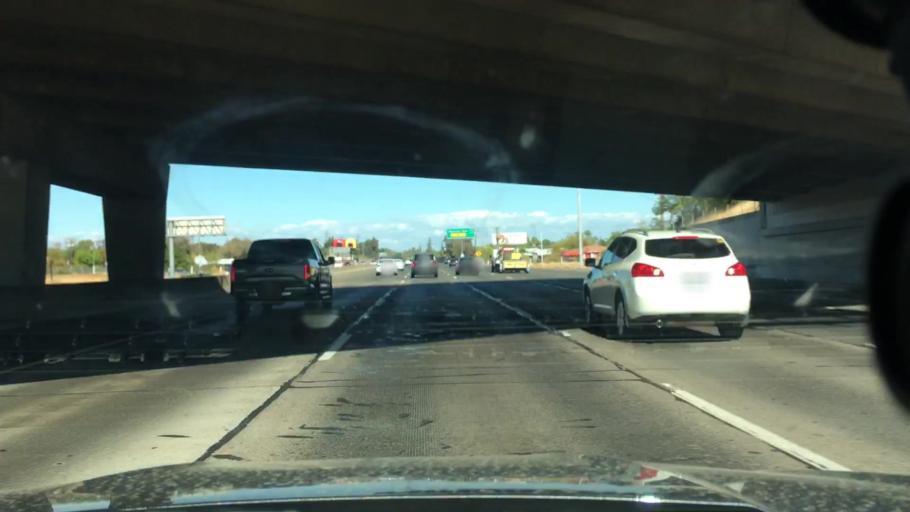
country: US
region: California
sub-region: Sacramento County
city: Arden-Arcade
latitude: 38.6141
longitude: -121.4298
